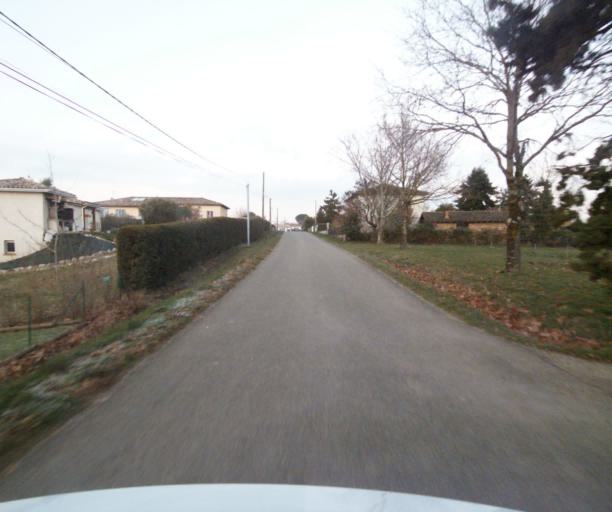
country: FR
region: Midi-Pyrenees
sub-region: Departement du Tarn-et-Garonne
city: Moissac
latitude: 44.1251
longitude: 1.0624
